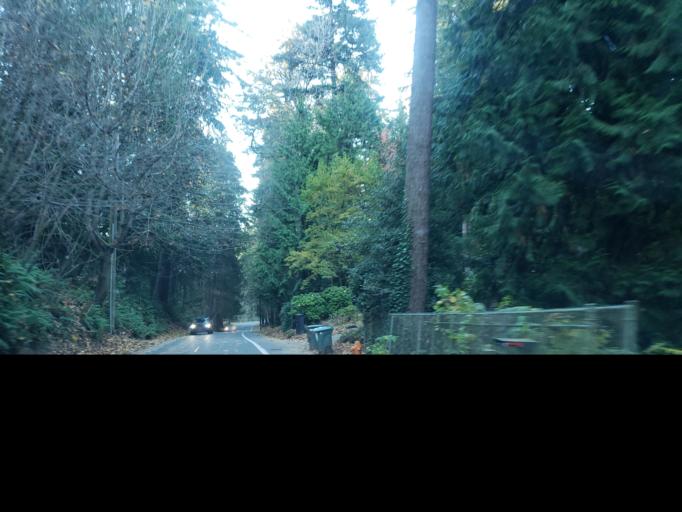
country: US
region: Washington
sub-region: Snohomish County
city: Woodway
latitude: 47.7904
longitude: -122.3771
